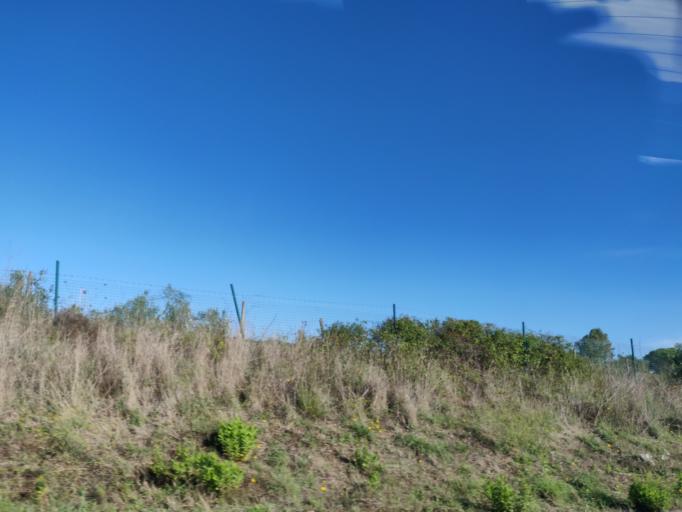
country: IT
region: Tuscany
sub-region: Provincia di Grosseto
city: Follonica
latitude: 42.9533
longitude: 10.7813
